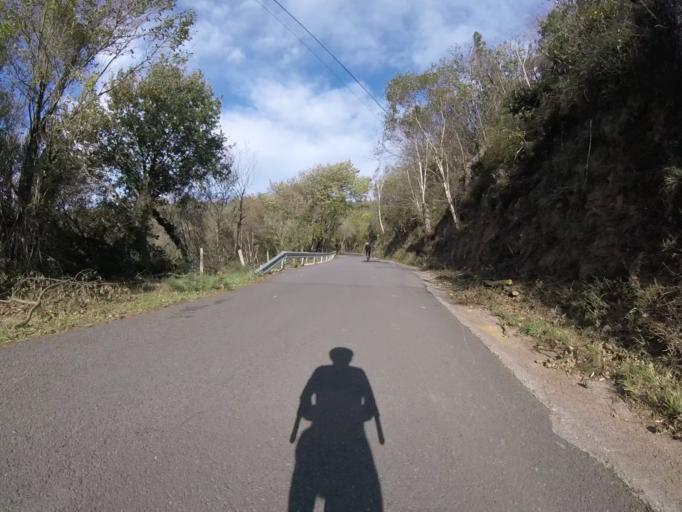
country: ES
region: Basque Country
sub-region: Provincia de Guipuzcoa
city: Orio
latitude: 43.2892
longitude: -2.1000
